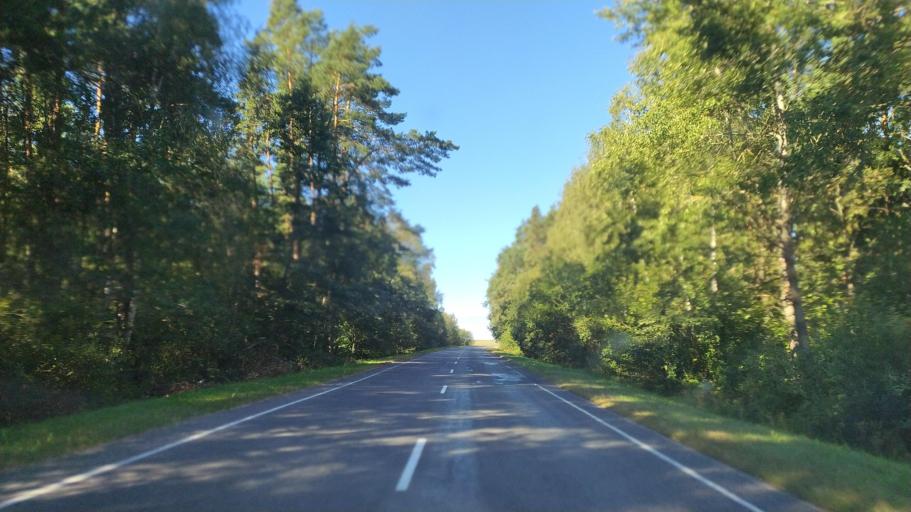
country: BY
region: Brest
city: Byaroza
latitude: 52.4847
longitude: 24.7658
